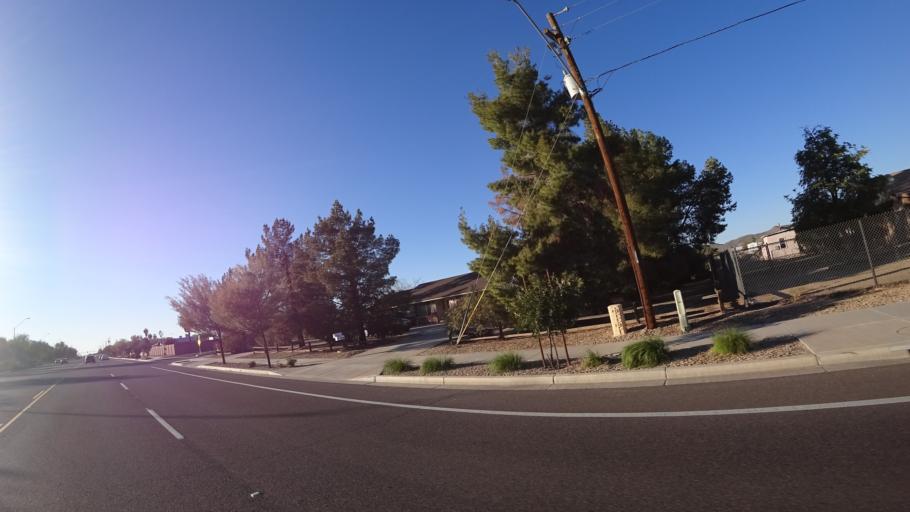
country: US
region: Arizona
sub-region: Maricopa County
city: Sun City
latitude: 33.6817
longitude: -112.2479
